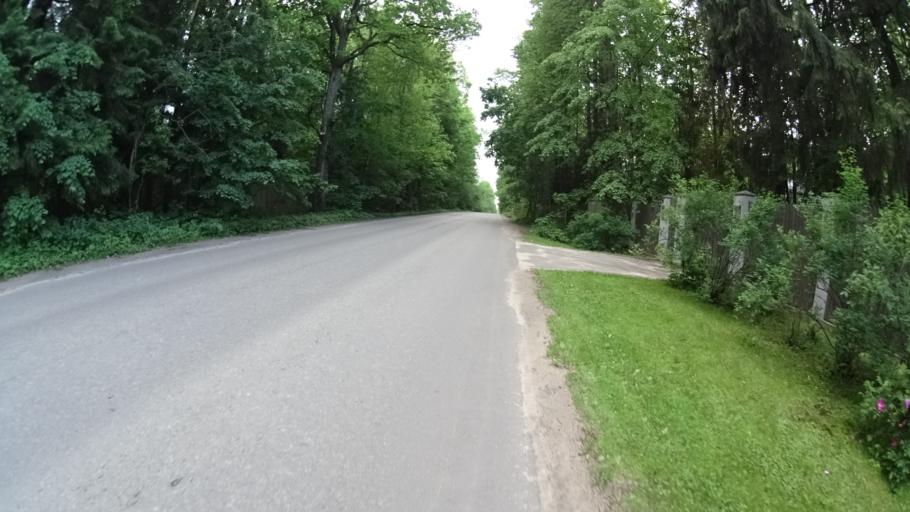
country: RU
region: Moskovskaya
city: Zelenogradskiy
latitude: 56.1181
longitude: 37.9266
